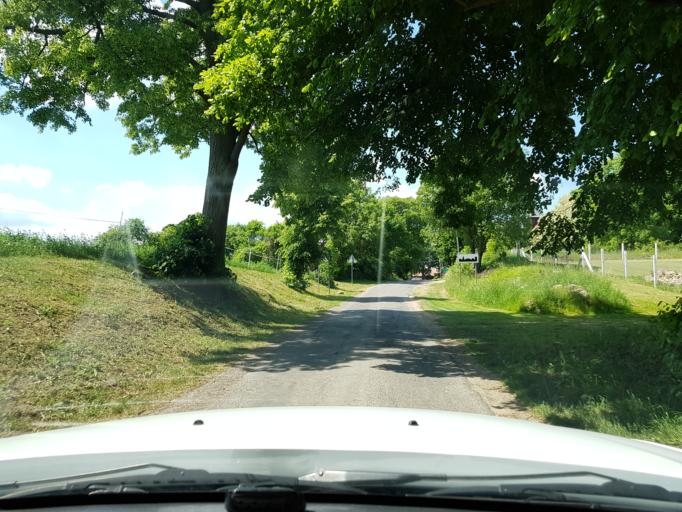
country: PL
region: West Pomeranian Voivodeship
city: Trzcinsko Zdroj
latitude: 52.9091
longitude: 14.6001
